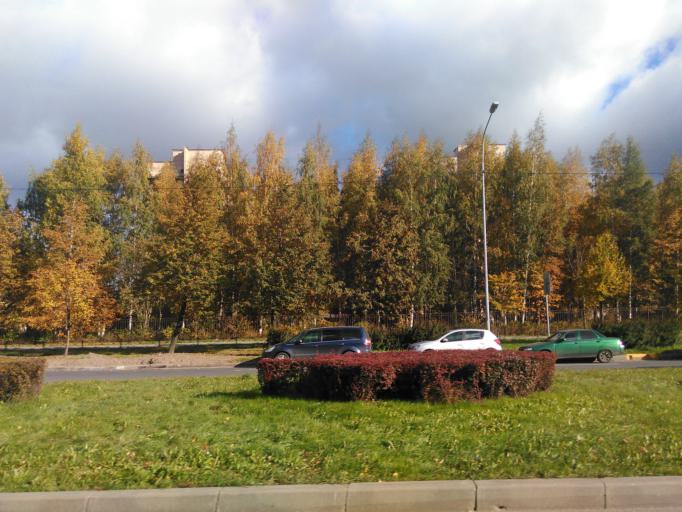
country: RU
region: St.-Petersburg
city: Krasnogvargeisky
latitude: 59.9273
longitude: 30.4867
